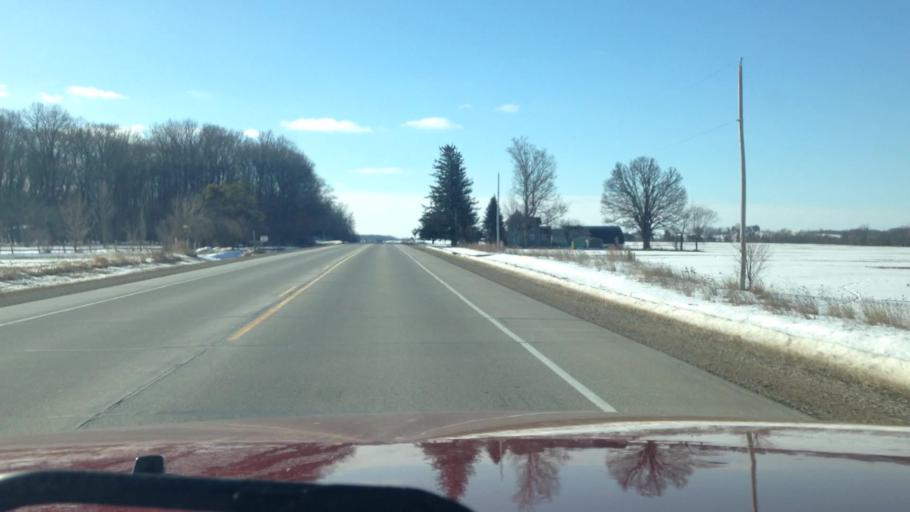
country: US
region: Wisconsin
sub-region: Waukesha County
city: Oconomowoc
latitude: 43.1885
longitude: -88.5082
